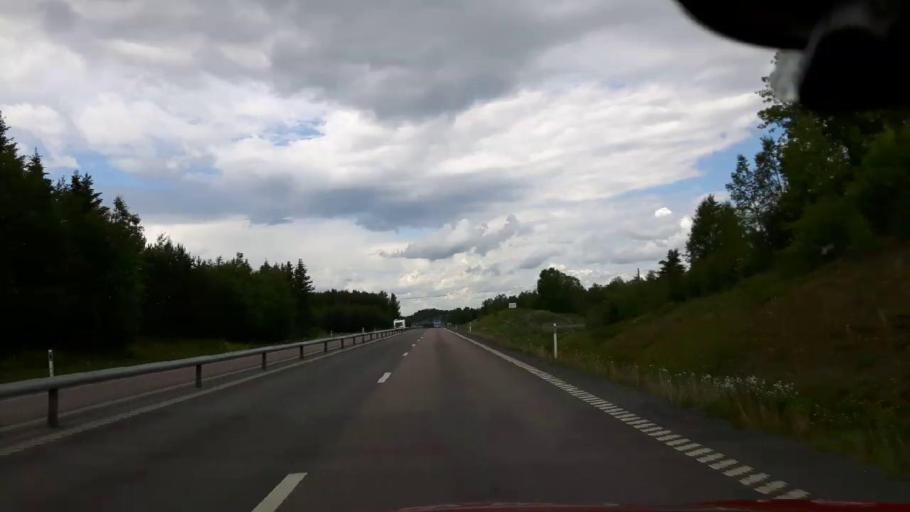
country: SE
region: Jaemtland
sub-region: Krokoms Kommun
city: Krokom
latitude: 63.2997
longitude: 14.4959
